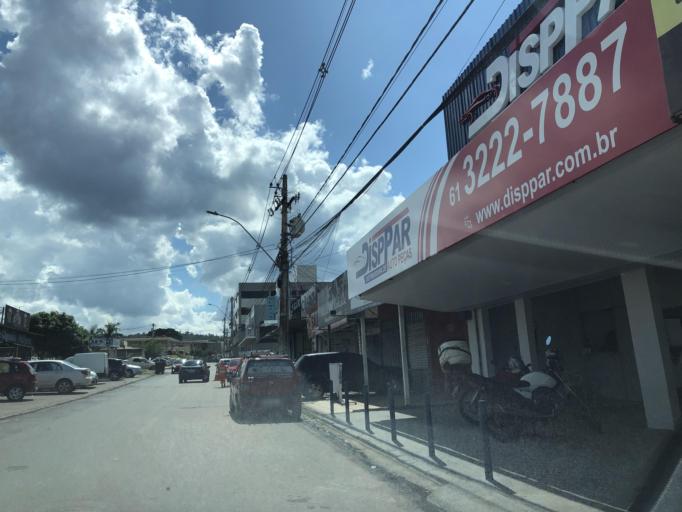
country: BR
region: Federal District
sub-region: Brasilia
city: Brasilia
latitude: -15.8987
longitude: -47.7811
